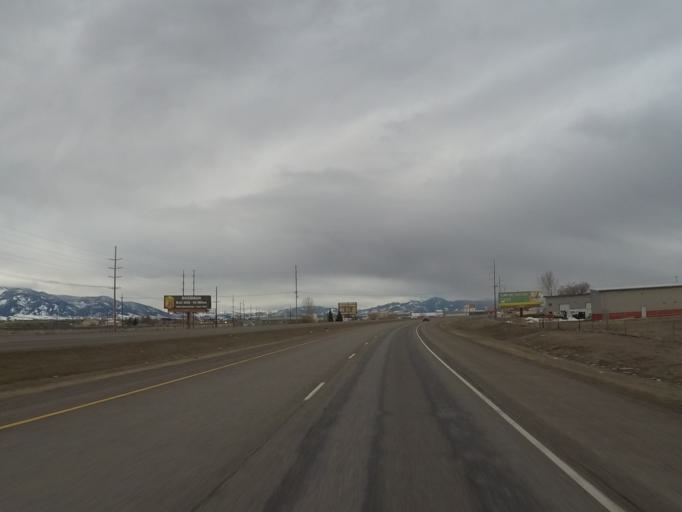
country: US
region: Montana
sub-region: Gallatin County
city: Belgrade
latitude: 45.7893
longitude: -111.2058
